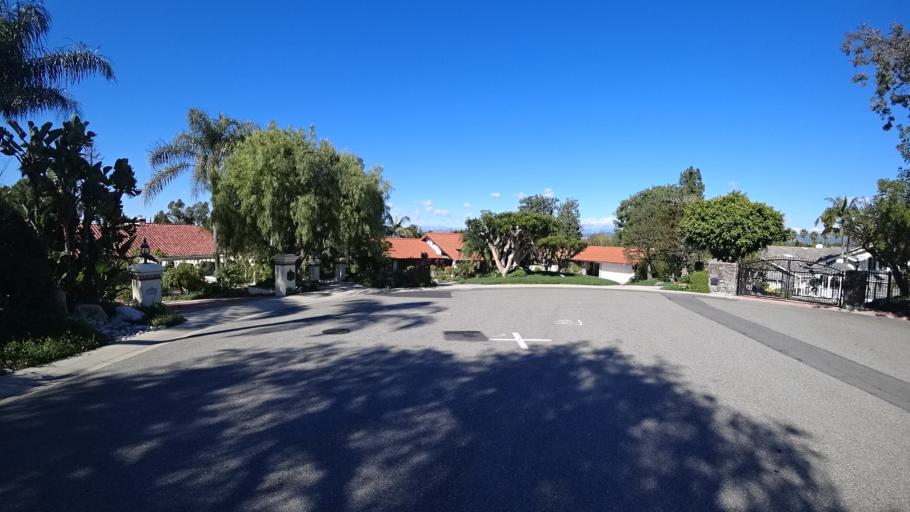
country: US
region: California
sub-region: Orange County
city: Villa Park
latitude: 33.8446
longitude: -117.8188
